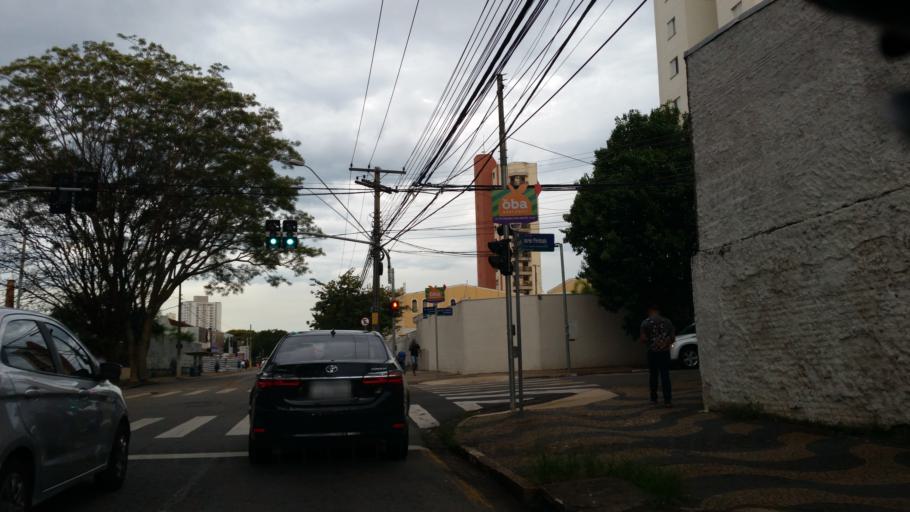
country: BR
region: Sao Paulo
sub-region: Campinas
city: Campinas
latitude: -22.9149
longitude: -47.0624
